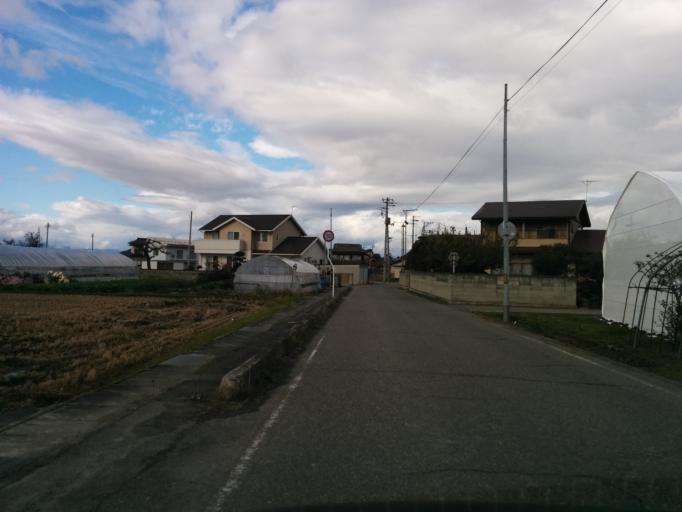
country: JP
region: Fukushima
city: Kitakata
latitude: 37.5060
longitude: 139.9056
